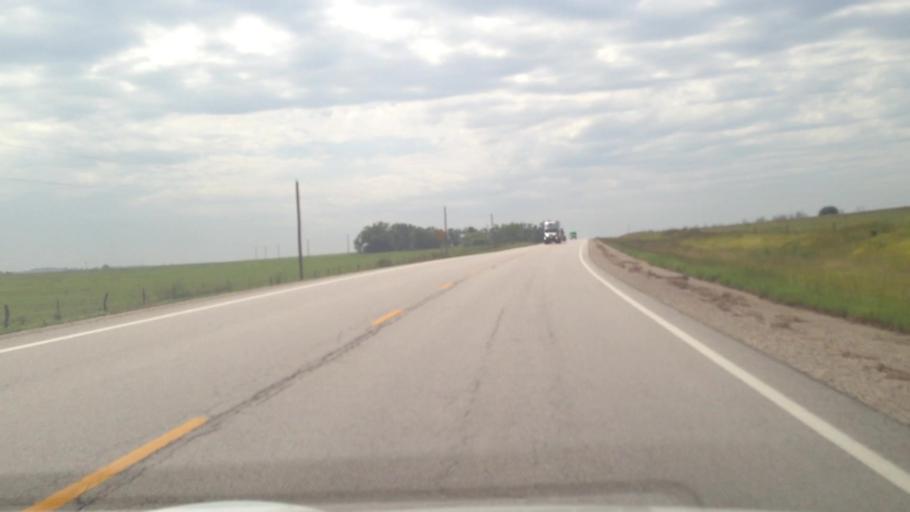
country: US
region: Kansas
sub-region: Anderson County
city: Garnett
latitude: 38.1887
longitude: -95.2412
